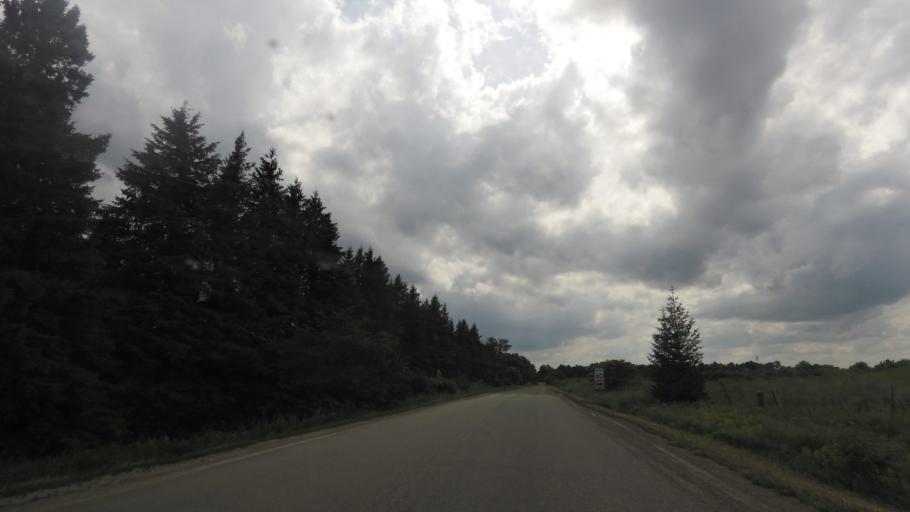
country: CA
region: Ontario
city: Orangeville
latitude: 43.8598
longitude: -79.9478
